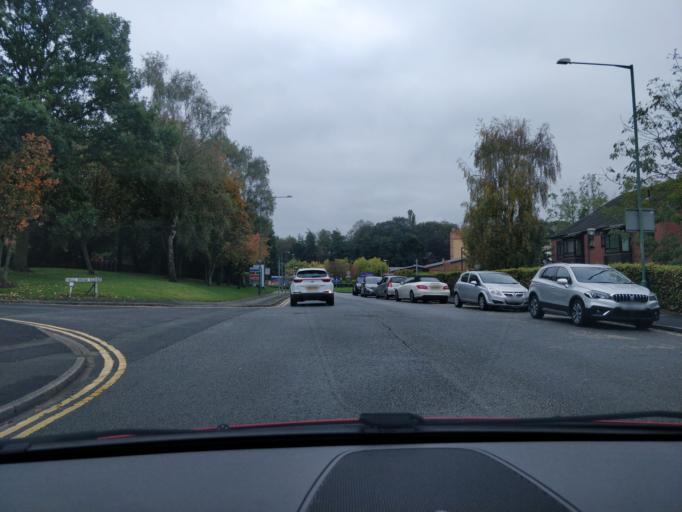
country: GB
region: England
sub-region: Lancashire
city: Ormskirk
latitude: 53.5655
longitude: -2.8698
